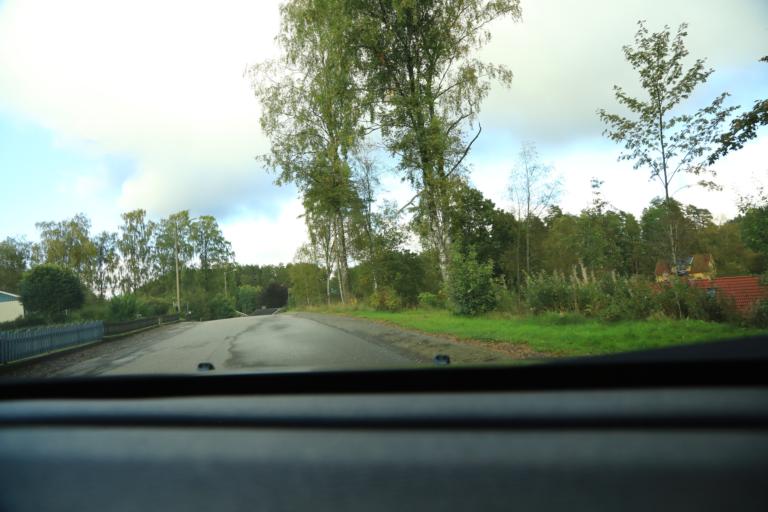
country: SE
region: Halland
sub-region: Halmstads Kommun
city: Getinge
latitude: 57.1283
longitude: 12.7133
